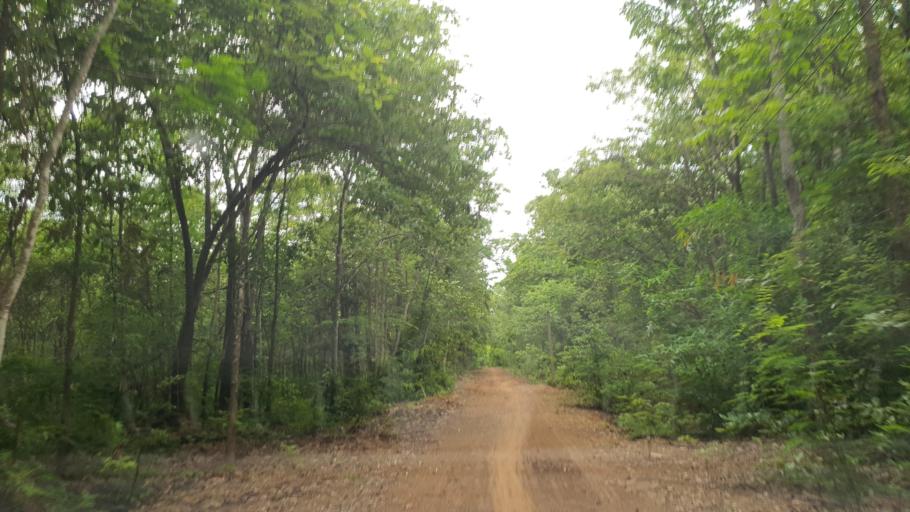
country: TH
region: Sukhothai
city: Thung Saliam
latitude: 17.2402
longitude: 99.5436
